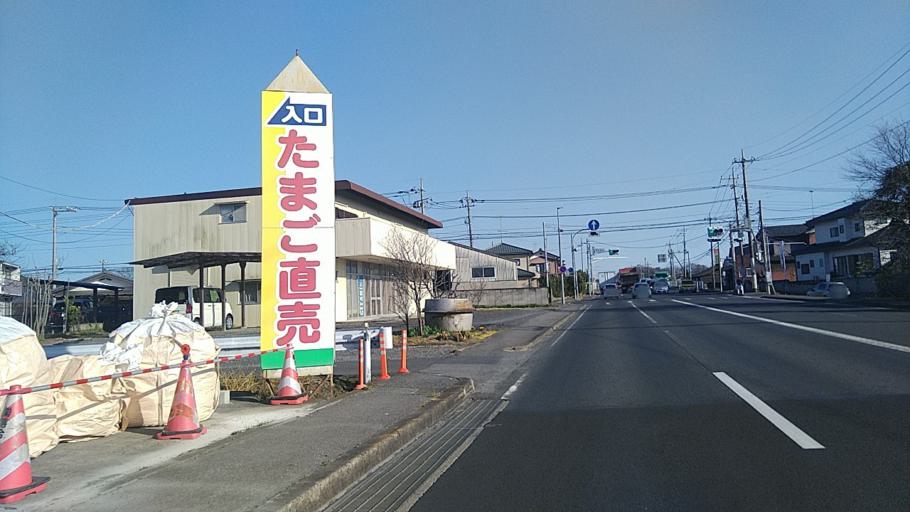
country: JP
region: Tochigi
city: Sano
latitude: 36.3373
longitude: 139.5781
